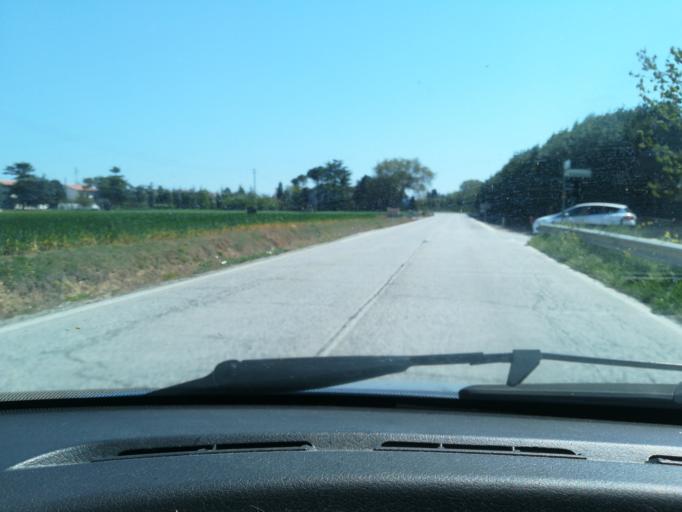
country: IT
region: The Marches
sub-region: Provincia di Ancona
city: Castelfidardo
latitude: 43.4528
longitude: 13.5285
